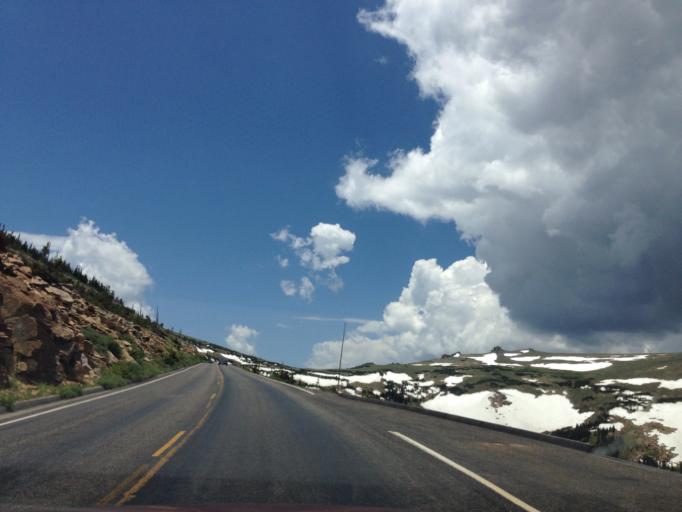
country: US
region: Colorado
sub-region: Larimer County
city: Estes Park
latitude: 40.3975
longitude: -105.6755
